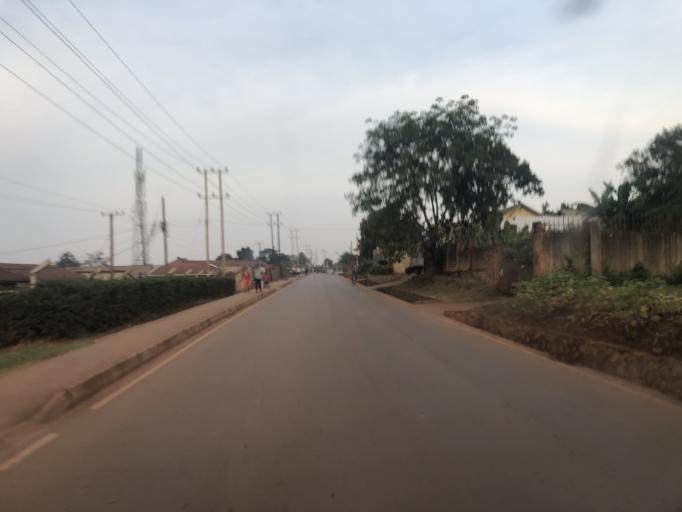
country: UG
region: Central Region
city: Kampala Central Division
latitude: 0.2917
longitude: 32.5343
